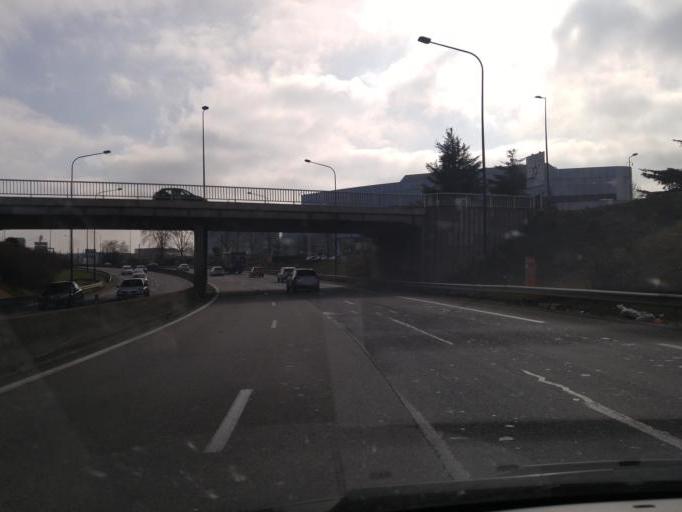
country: FR
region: Midi-Pyrenees
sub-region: Departement de la Haute-Garonne
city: Blagnac
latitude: 43.6268
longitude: 1.3840
